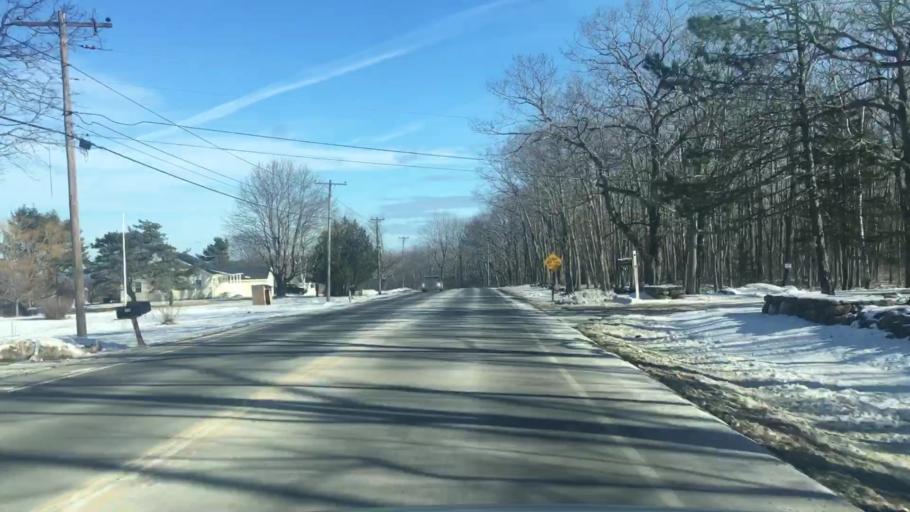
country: US
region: Maine
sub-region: Knox County
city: Rockland
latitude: 44.1297
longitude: -69.1067
